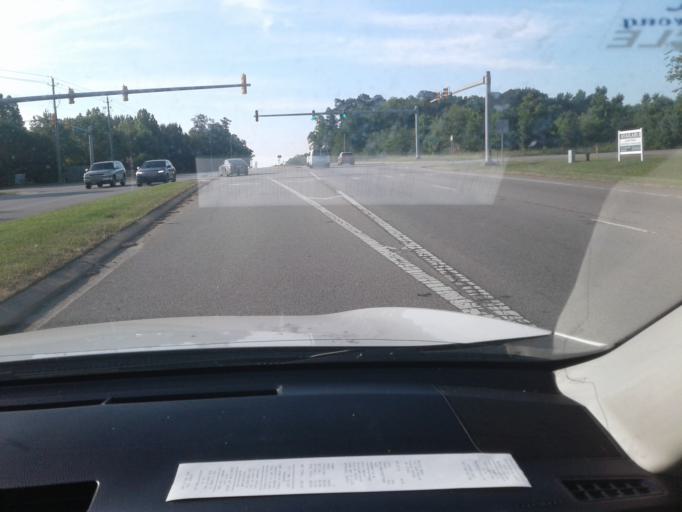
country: US
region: North Carolina
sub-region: Wake County
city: Holly Springs
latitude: 35.6336
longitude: -78.8281
